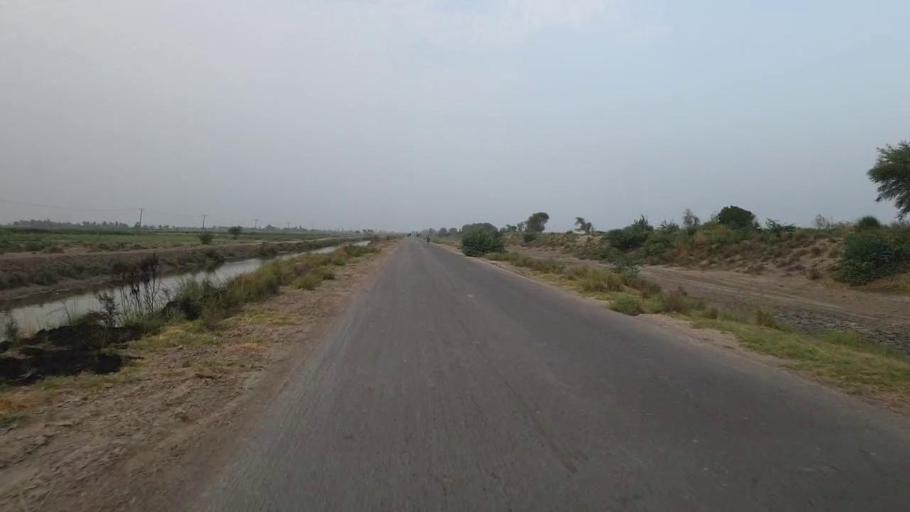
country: PK
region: Sindh
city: Daur
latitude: 26.4417
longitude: 68.2783
